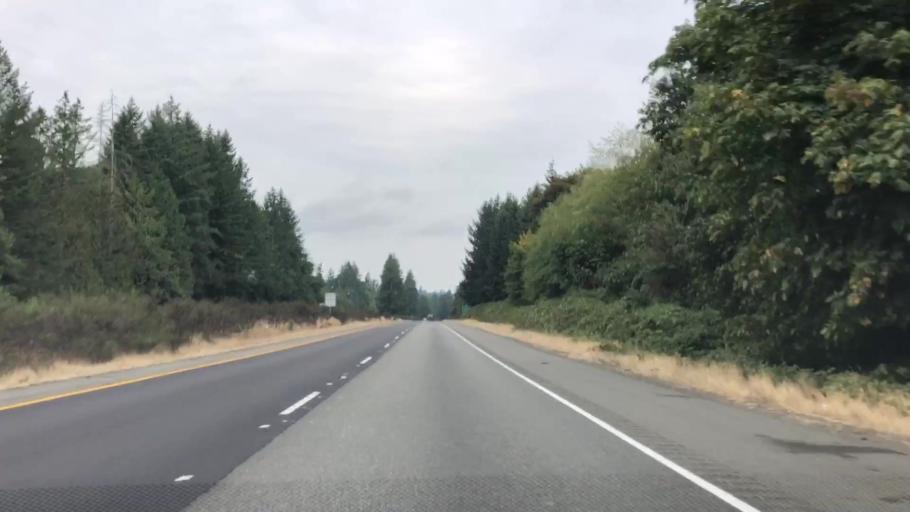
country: US
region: Washington
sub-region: Kitsap County
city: Bethel
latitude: 47.5132
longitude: -122.6538
